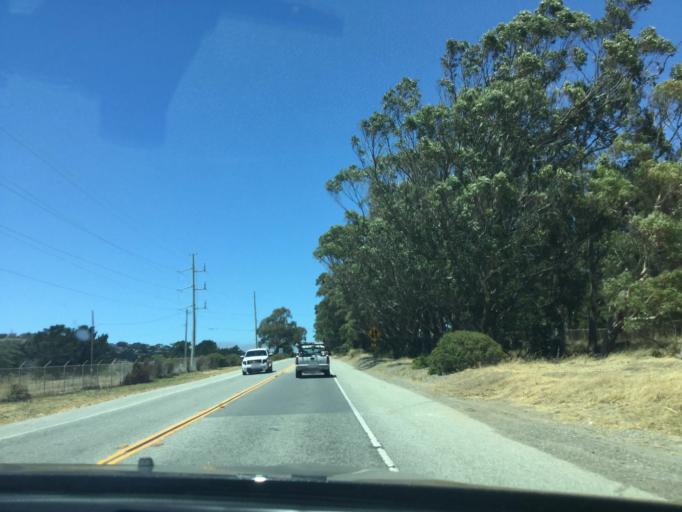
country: US
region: California
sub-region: San Mateo County
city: San Bruno
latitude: 37.6128
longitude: -122.4366
